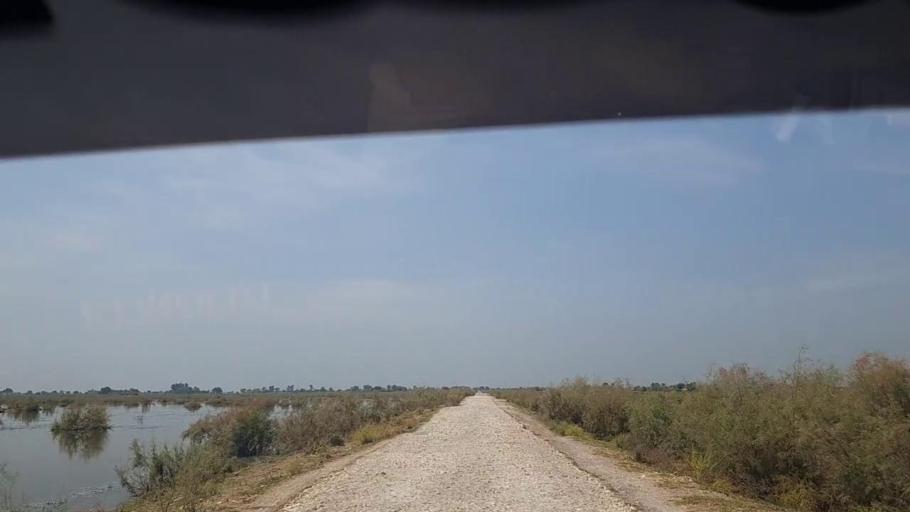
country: PK
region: Sindh
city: Thul
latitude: 28.1685
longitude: 68.7616
